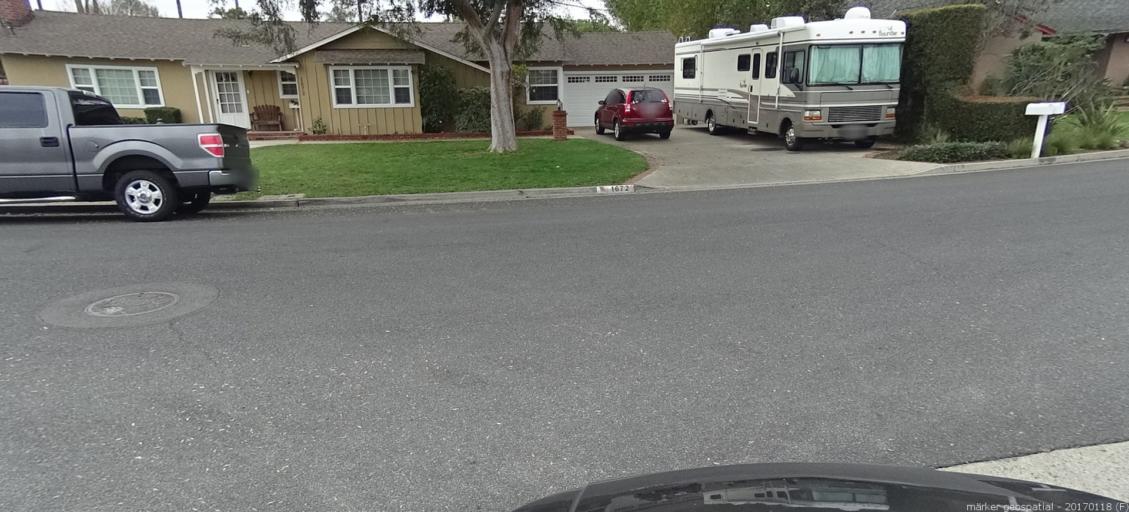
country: US
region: California
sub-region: Orange County
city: North Tustin
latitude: 33.7476
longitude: -117.7974
